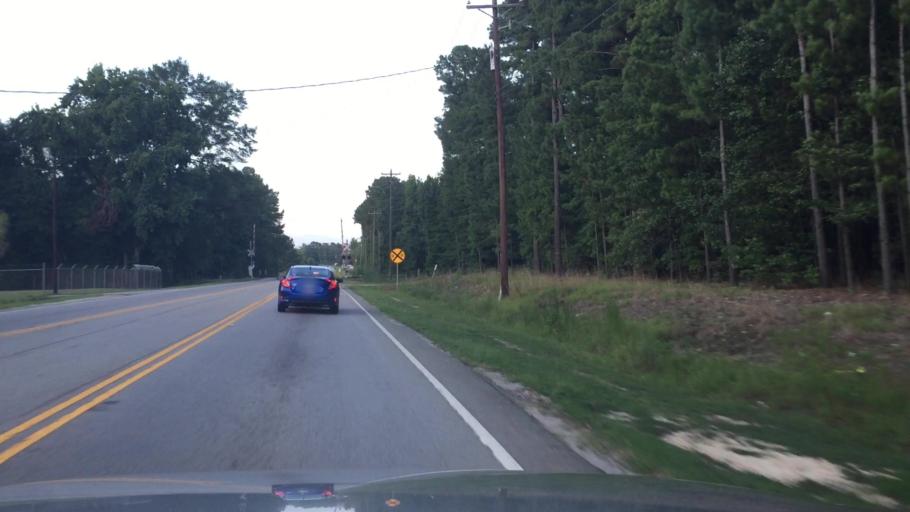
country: US
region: South Carolina
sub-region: Richland County
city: Hopkins
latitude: 33.9472
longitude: -80.9347
